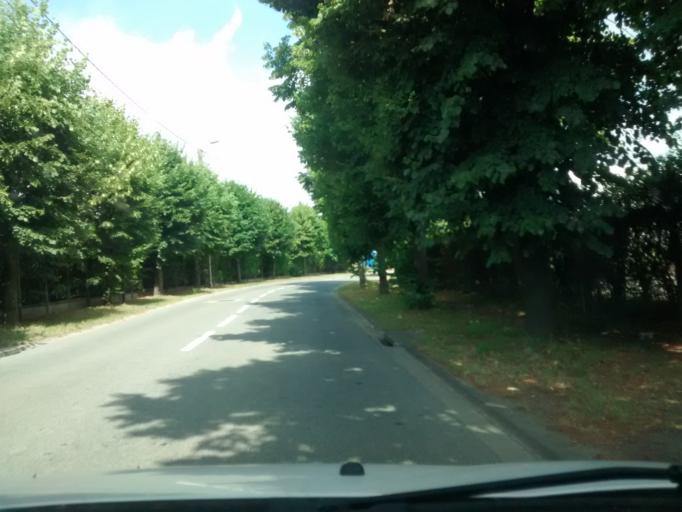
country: FR
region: Brittany
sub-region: Departement d'Ille-et-Vilaine
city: Chantepie
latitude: 48.1024
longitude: -1.6312
